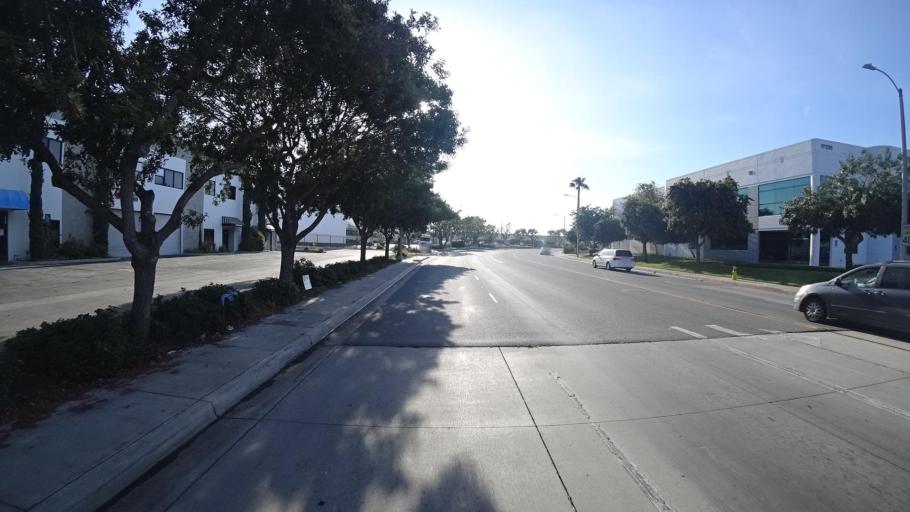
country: US
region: California
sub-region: Los Angeles County
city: La Puente
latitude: 34.0039
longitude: -117.9292
